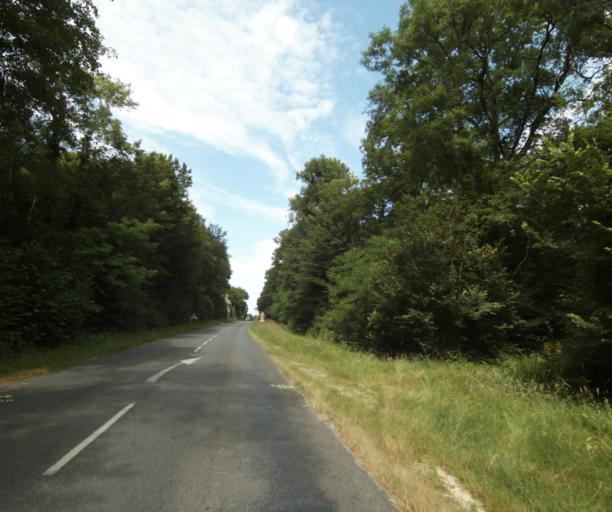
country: FR
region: Ile-de-France
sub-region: Departement de Seine-et-Marne
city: Chailly-en-Biere
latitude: 48.4869
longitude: 2.6285
